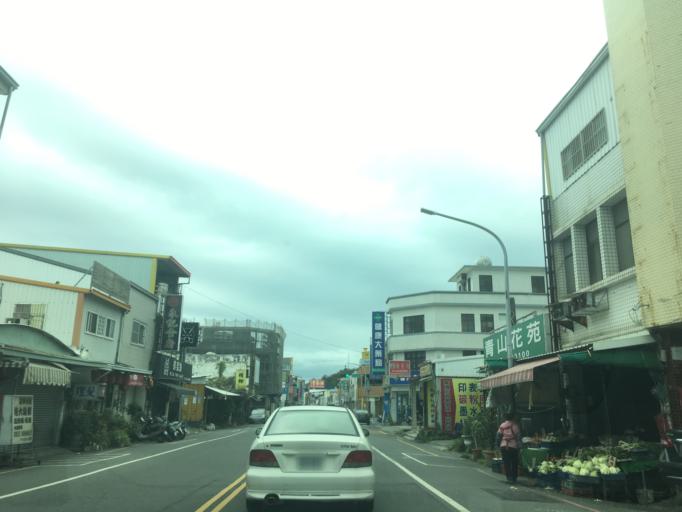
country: TW
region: Taiwan
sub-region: Taitung
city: Taitung
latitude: 22.7609
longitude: 121.1386
